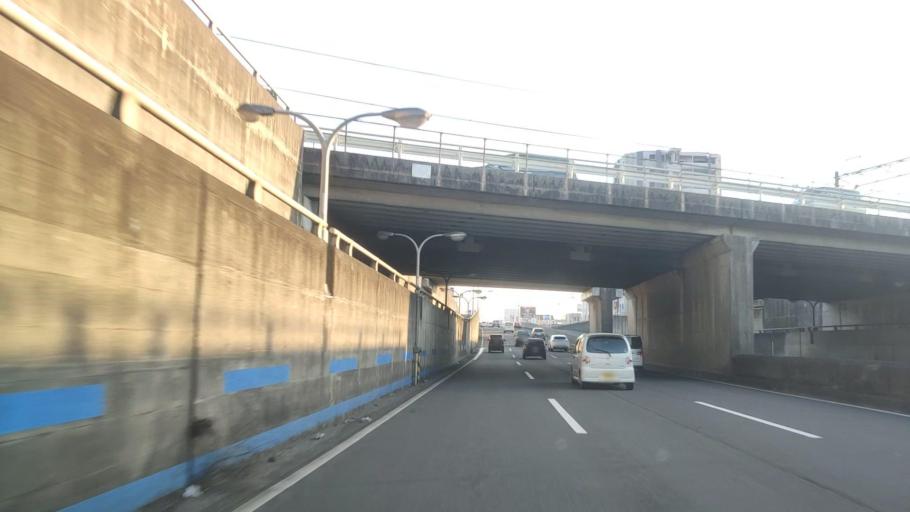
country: JP
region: Gifu
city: Gifu-shi
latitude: 35.4058
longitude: 136.7268
